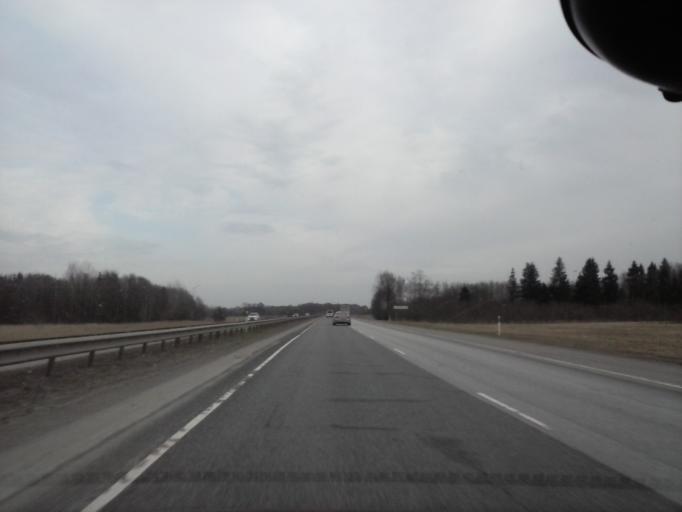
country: EE
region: Harju
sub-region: Rae vald
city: Jueri
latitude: 59.3436
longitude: 24.8972
